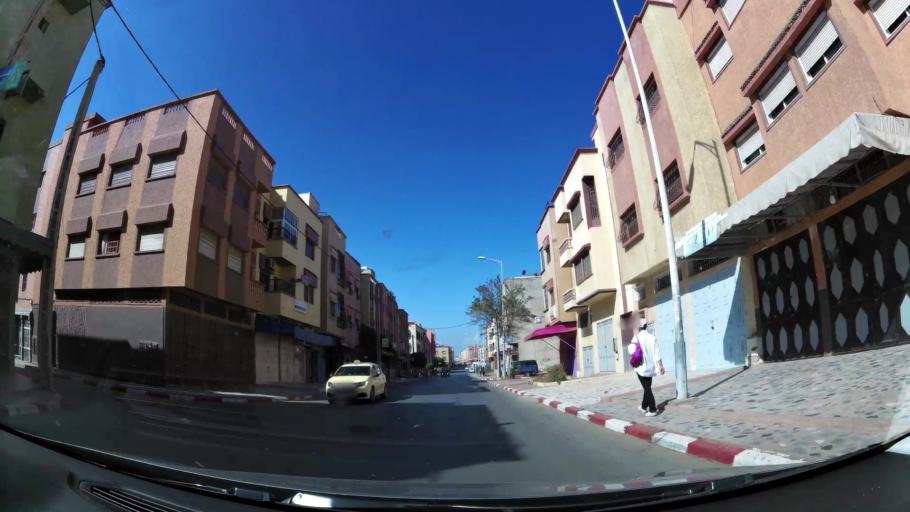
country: MA
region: Rabat-Sale-Zemmour-Zaer
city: Sale
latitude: 34.0715
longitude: -6.7965
